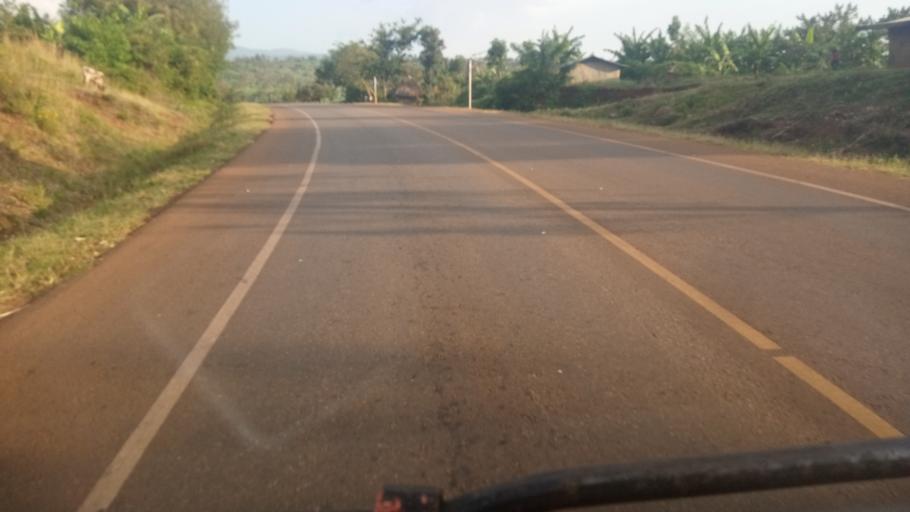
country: UG
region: Eastern Region
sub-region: Sironko District
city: Sironko
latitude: 1.3335
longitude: 34.3223
